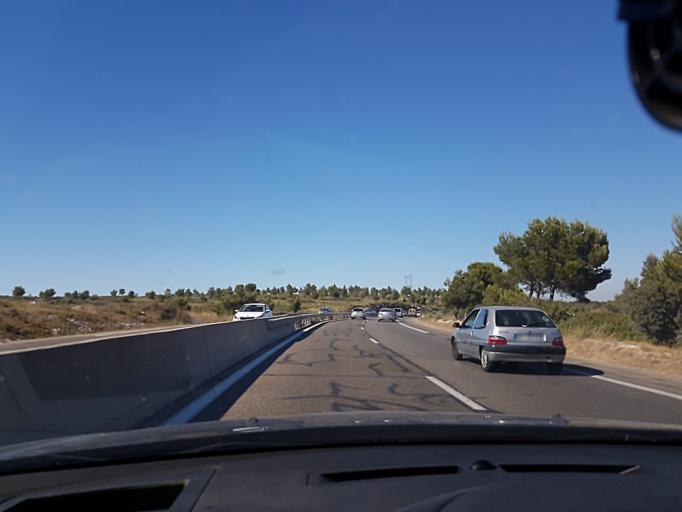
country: FR
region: Provence-Alpes-Cote d'Azur
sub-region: Departement des Bouches-du-Rhone
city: Carry-le-Rouet
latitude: 43.3510
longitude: 5.1700
